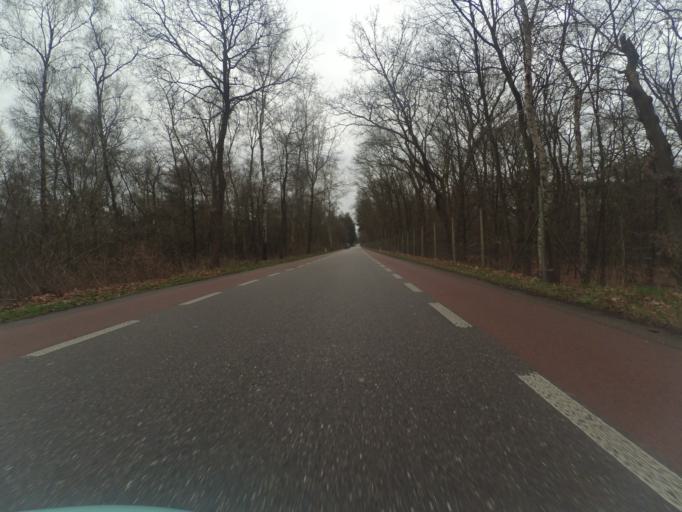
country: NL
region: Gelderland
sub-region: Gemeente Arnhem
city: Gulden Bodem
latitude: 52.0416
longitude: 5.9043
